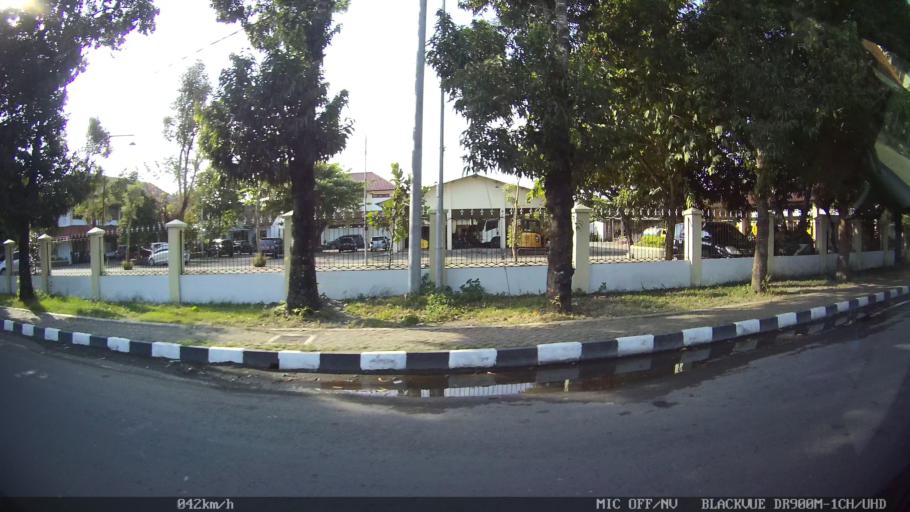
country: ID
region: Daerah Istimewa Yogyakarta
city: Bantul
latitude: -7.9056
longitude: 110.3173
